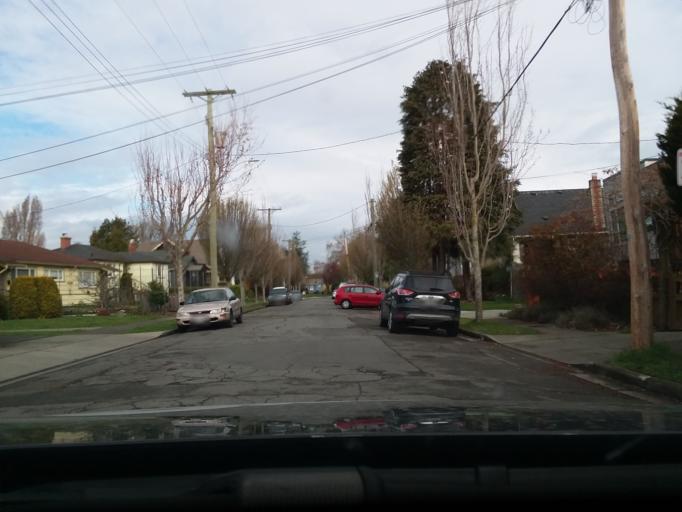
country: CA
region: British Columbia
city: Oak Bay
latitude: 48.4298
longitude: -123.3316
